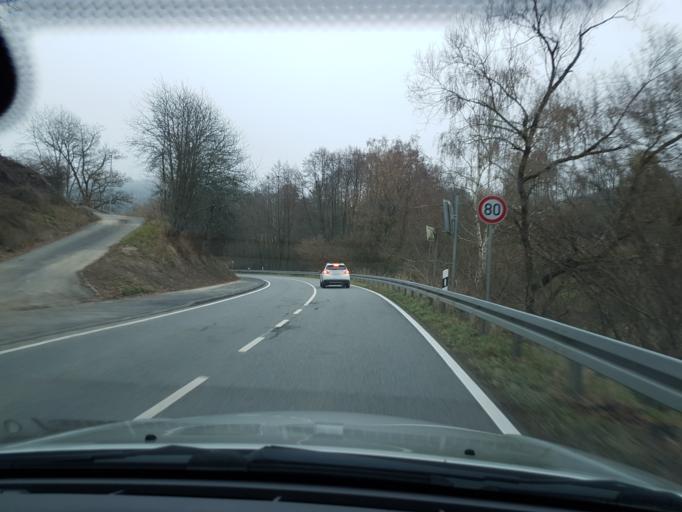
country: DE
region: Hesse
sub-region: Regierungsbezirk Darmstadt
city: Schlangenbad
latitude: 50.1084
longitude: 8.0913
